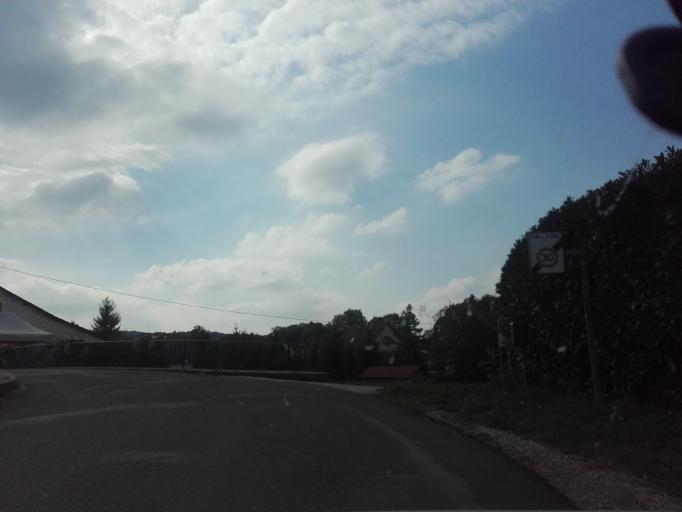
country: FR
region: Bourgogne
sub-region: Departement de Saone-et-Loire
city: Chagny
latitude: 46.9065
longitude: 4.7211
